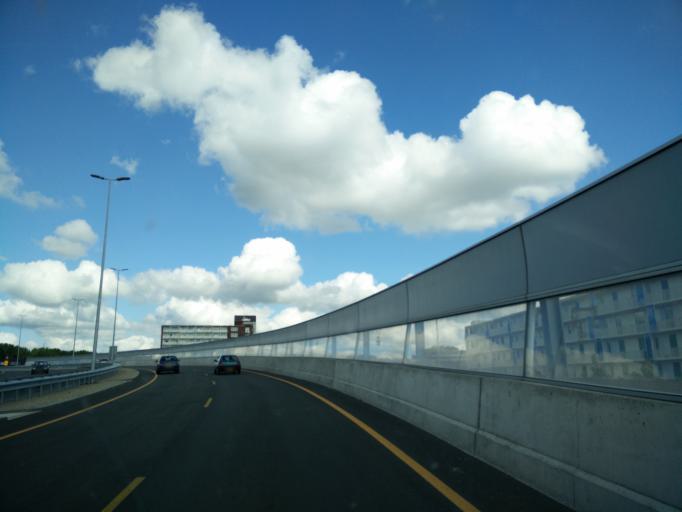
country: NL
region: Groningen
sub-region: Gemeente Groningen
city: Korrewegwijk
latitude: 53.2376
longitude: 6.5637
